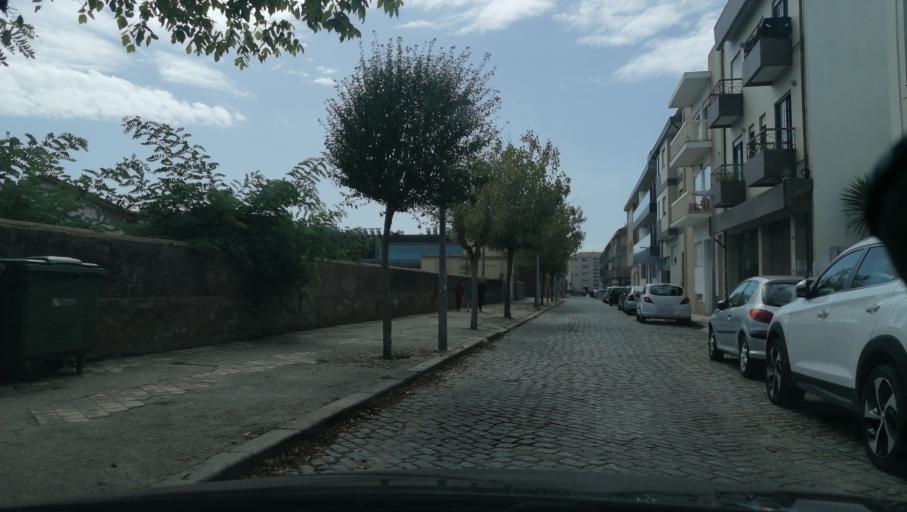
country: PT
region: Aveiro
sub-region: Espinho
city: Espinho
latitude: 41.0030
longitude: -8.6409
